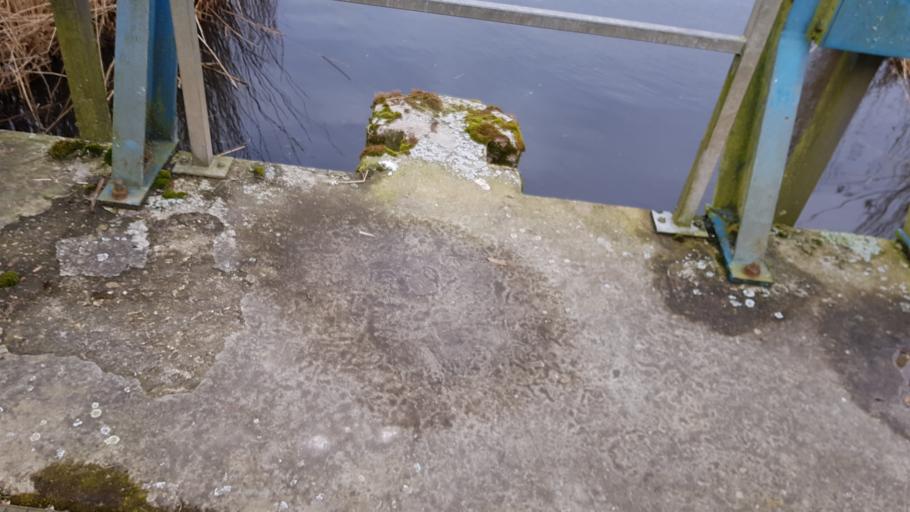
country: NL
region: North Holland
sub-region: Gemeente Blaricum
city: Blaricum
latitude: 52.2776
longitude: 5.3054
